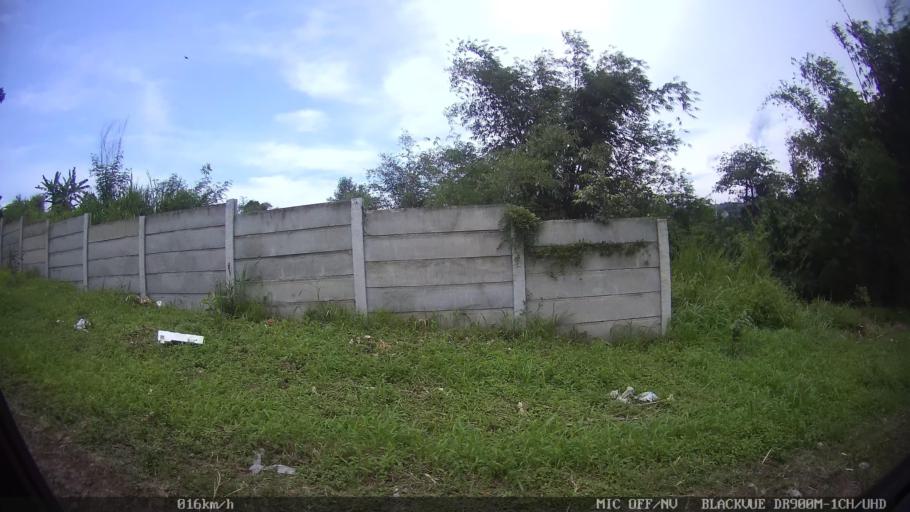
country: ID
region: Lampung
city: Bandarlampung
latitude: -5.4062
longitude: 105.2007
